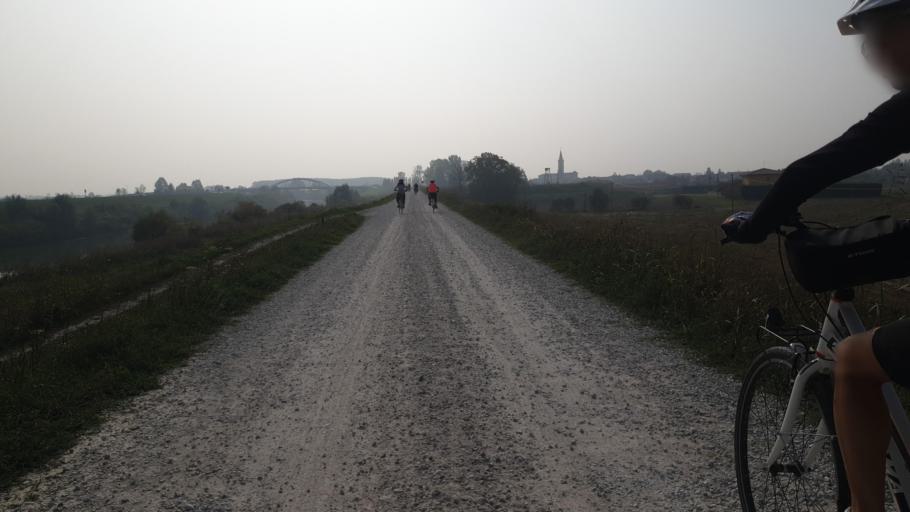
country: IT
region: Veneto
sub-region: Provincia di Padova
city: Corte
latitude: 45.3167
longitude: 12.0733
